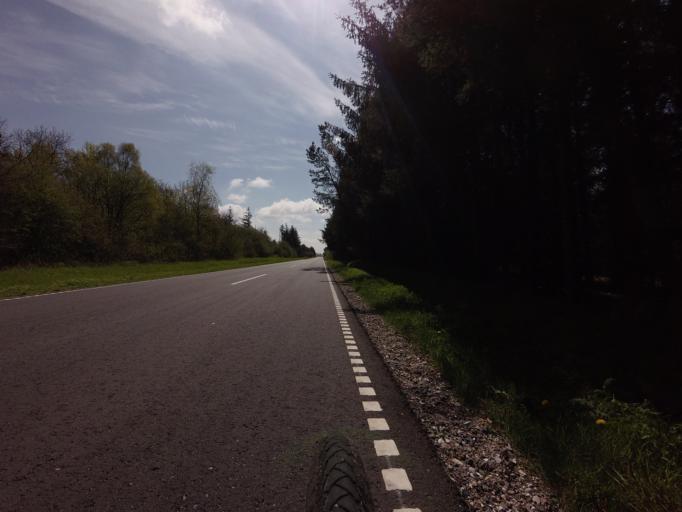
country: DK
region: North Denmark
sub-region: Jammerbugt Kommune
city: Brovst
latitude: 57.1589
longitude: 9.5759
